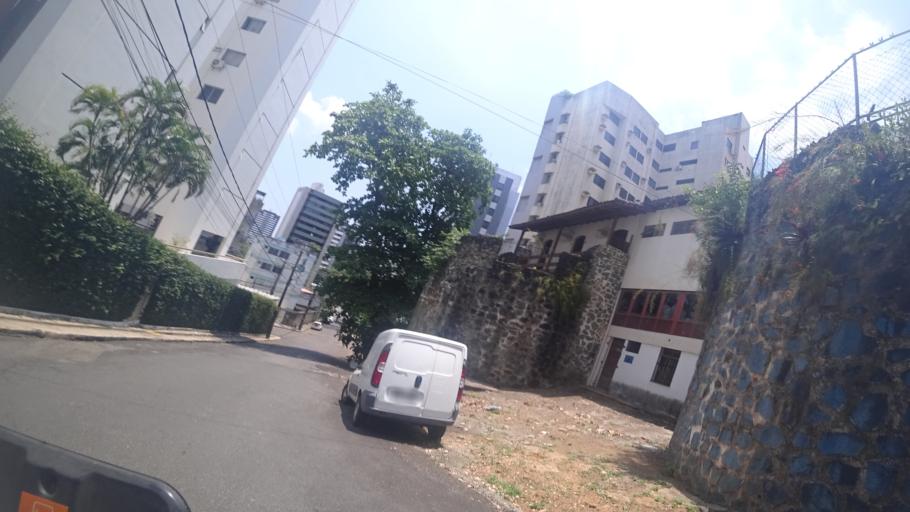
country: BR
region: Bahia
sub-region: Salvador
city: Salvador
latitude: -12.9930
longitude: -38.4522
